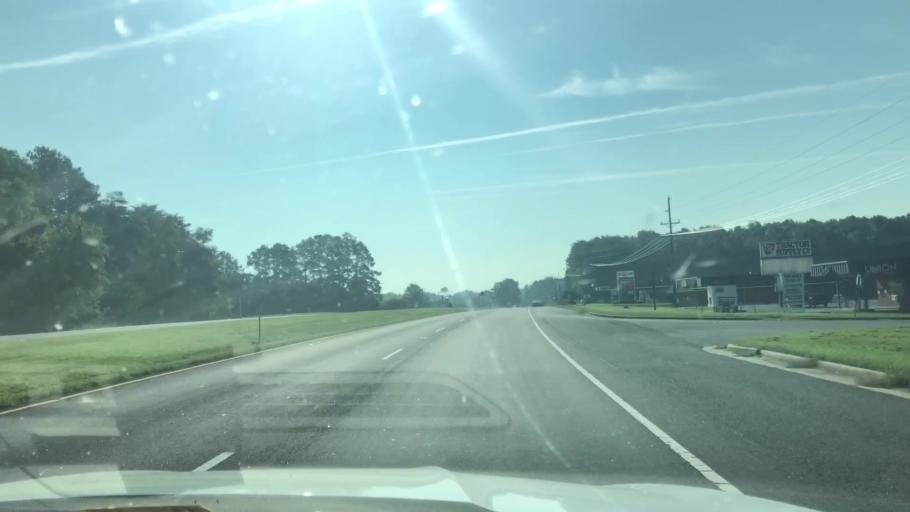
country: US
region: Virginia
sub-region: Richmond County
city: Warsaw
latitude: 37.9648
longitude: -76.7860
